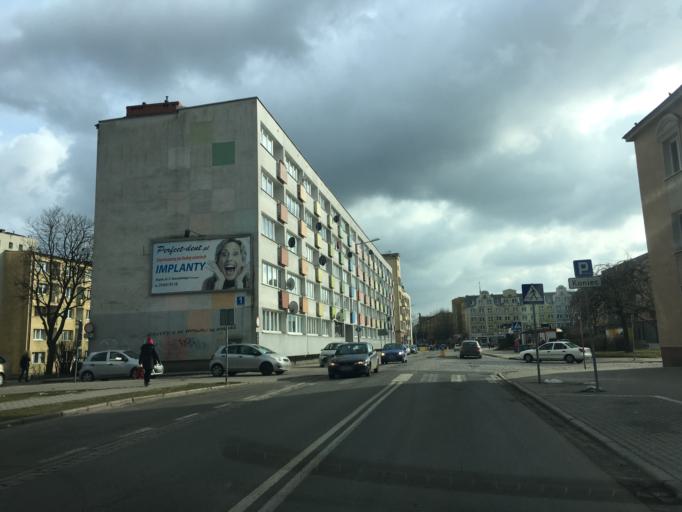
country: PL
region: Pomeranian Voivodeship
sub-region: Slupsk
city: Slupsk
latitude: 54.4682
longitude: 17.0308
